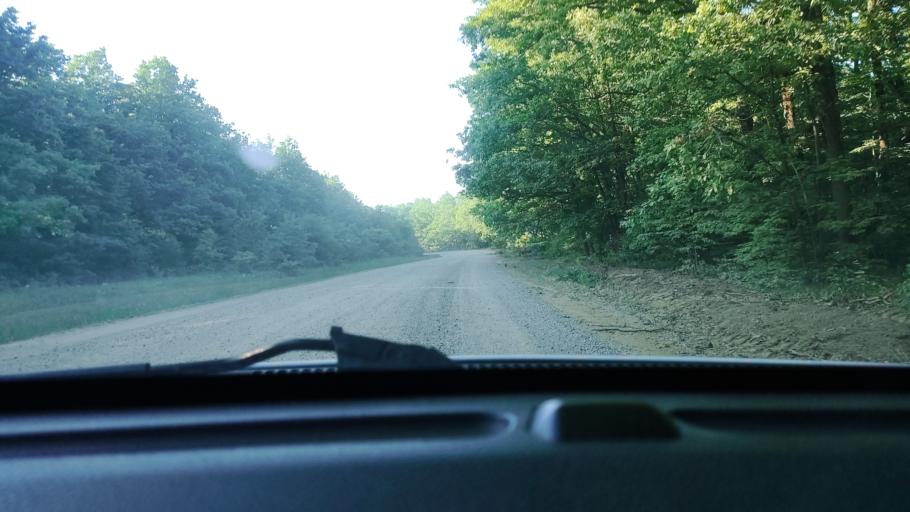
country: RU
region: Krasnodarskiy
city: Novodmitriyevskaya
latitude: 44.7164
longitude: 38.9915
